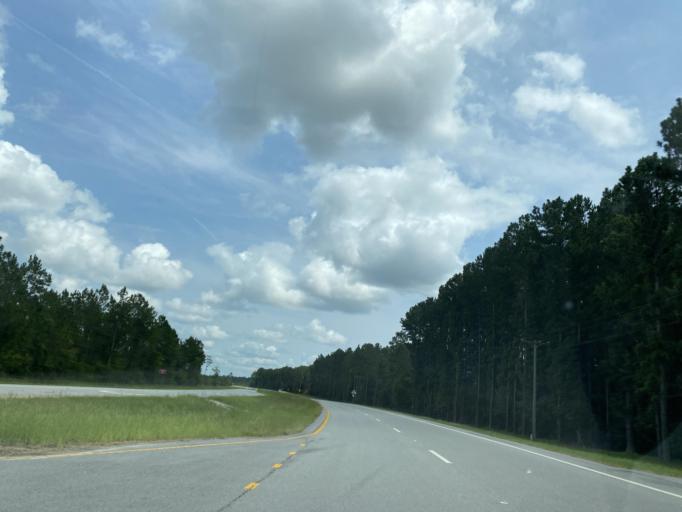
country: US
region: Georgia
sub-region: Ware County
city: Deenwood
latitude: 31.2760
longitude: -82.4493
